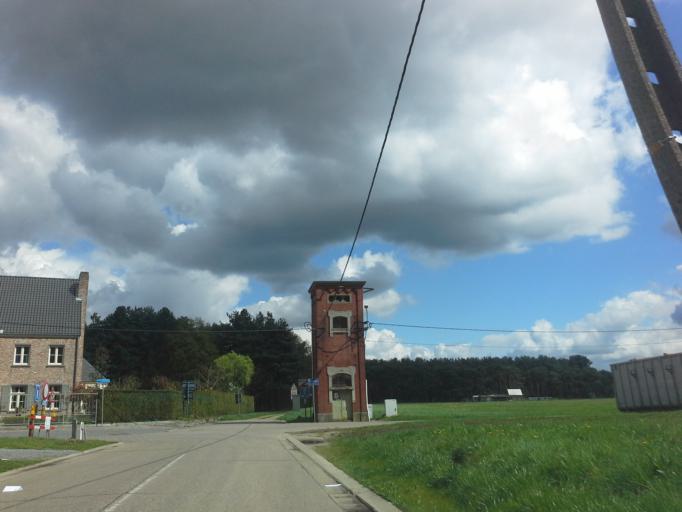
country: BE
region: Flanders
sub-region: Provincie Antwerpen
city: Meerhout
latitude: 51.1235
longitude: 5.0482
